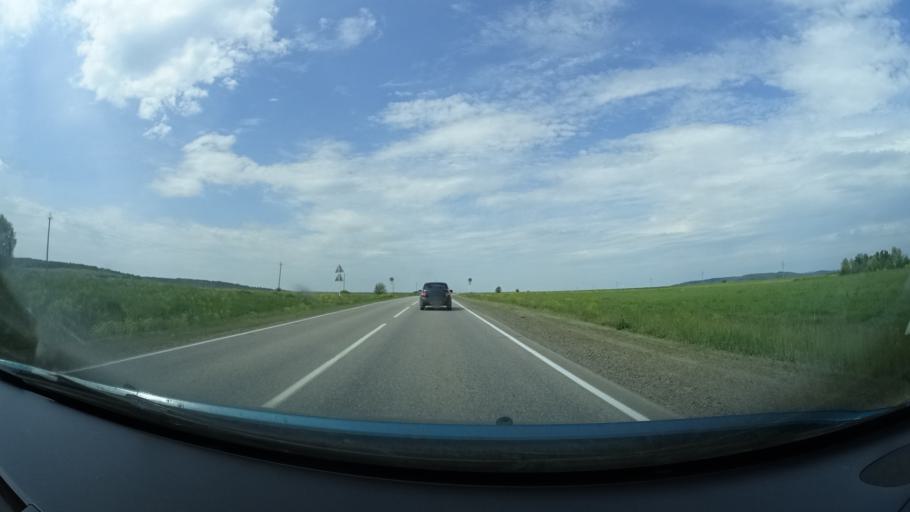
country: RU
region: Perm
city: Barda
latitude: 57.0326
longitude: 55.5492
